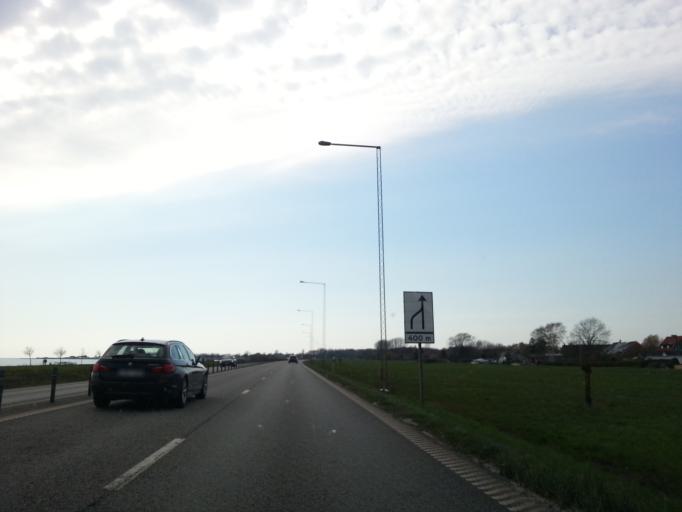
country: SE
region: Skane
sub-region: Trelleborgs Kommun
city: Trelleborg
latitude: 55.3761
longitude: 13.1130
